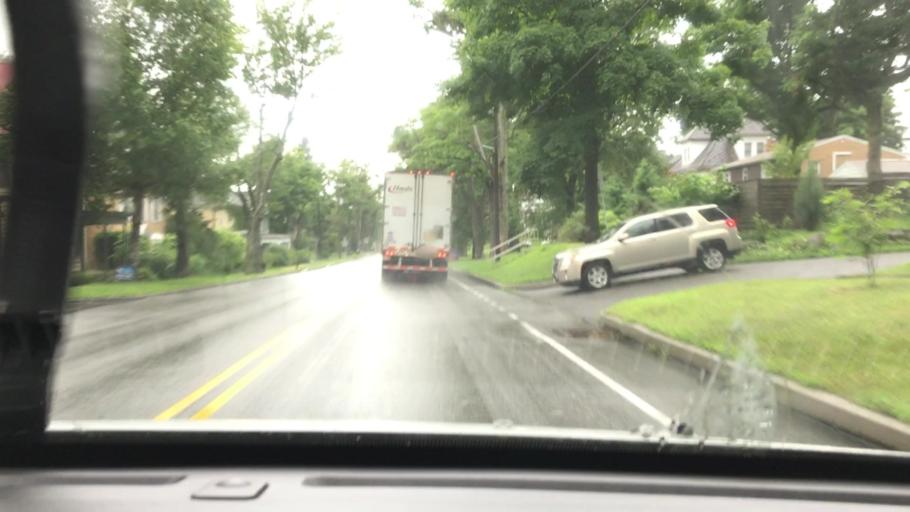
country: US
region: Pennsylvania
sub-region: Centre County
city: Philipsburg
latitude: 40.8940
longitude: -78.2184
